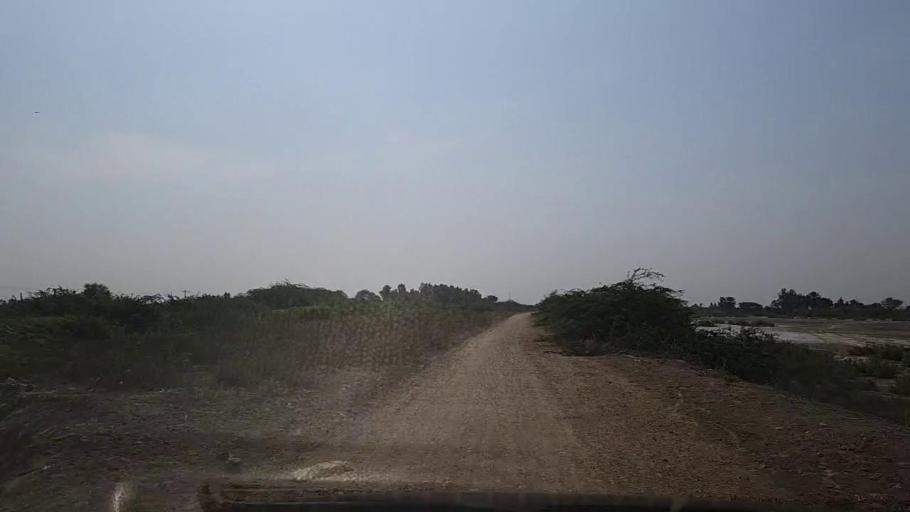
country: PK
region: Sindh
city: Thatta
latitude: 24.7805
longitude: 67.8279
